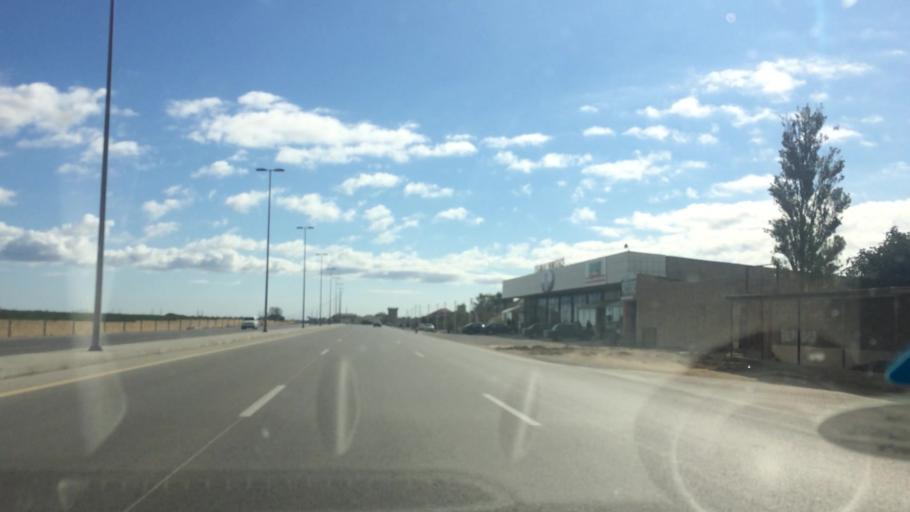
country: AZ
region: Baki
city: Qala
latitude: 40.4488
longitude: 50.1610
